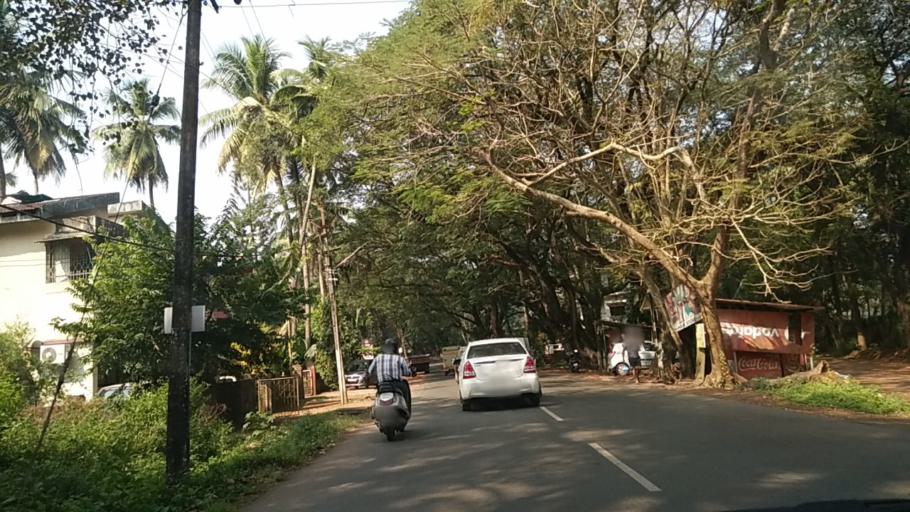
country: IN
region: Goa
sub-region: North Goa
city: Jua
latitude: 15.5004
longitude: 73.9014
